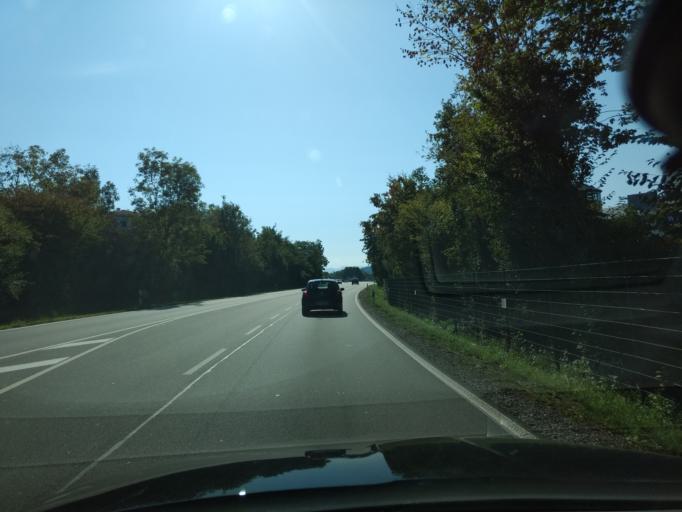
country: DE
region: Bavaria
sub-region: Upper Bavaria
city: Wolfratshausen
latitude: 47.9059
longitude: 11.4323
